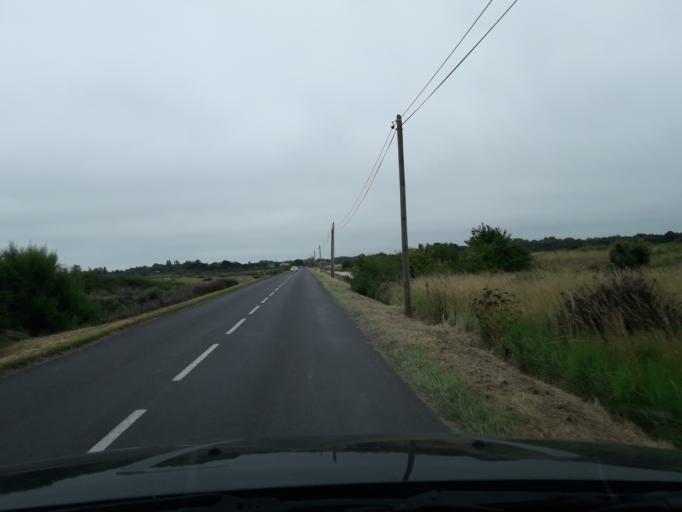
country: FR
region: Poitou-Charentes
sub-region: Departement de la Charente-Maritime
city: Boyard-Ville
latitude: 45.9597
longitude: -1.2491
